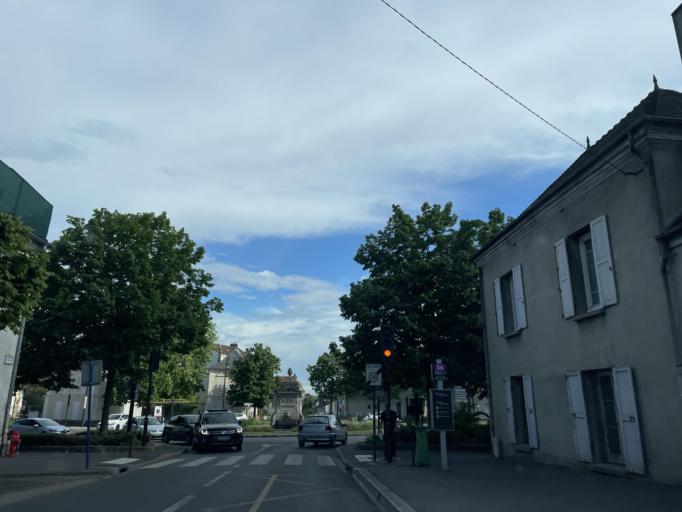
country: FR
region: Ile-de-France
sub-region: Departement du Val-d'Oise
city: Arnouville
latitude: 48.9807
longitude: 2.4232
